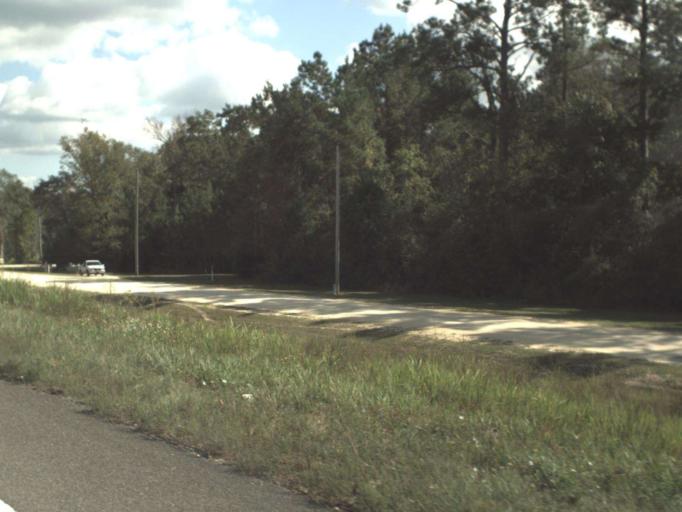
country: US
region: Florida
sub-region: Bay County
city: Laguna Beach
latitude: 30.4520
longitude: -85.9011
